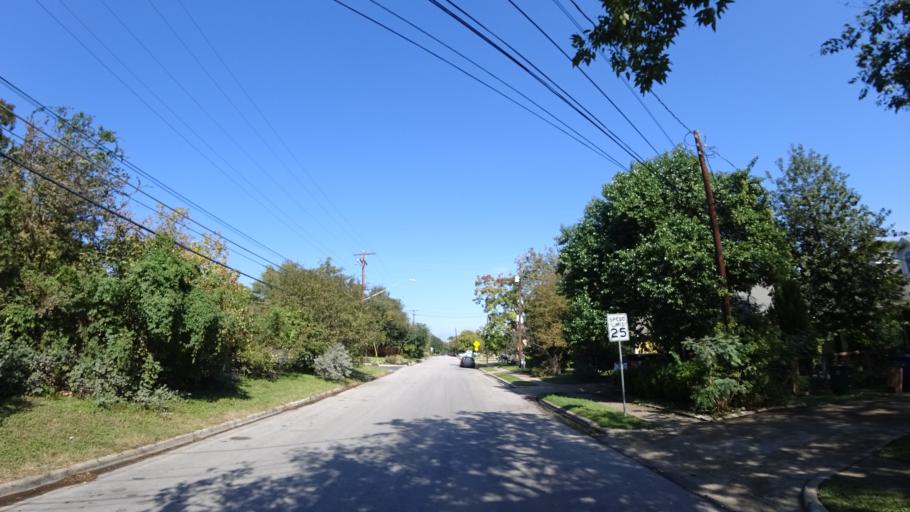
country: US
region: Texas
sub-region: Travis County
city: Austin
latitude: 30.2510
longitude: -97.7690
